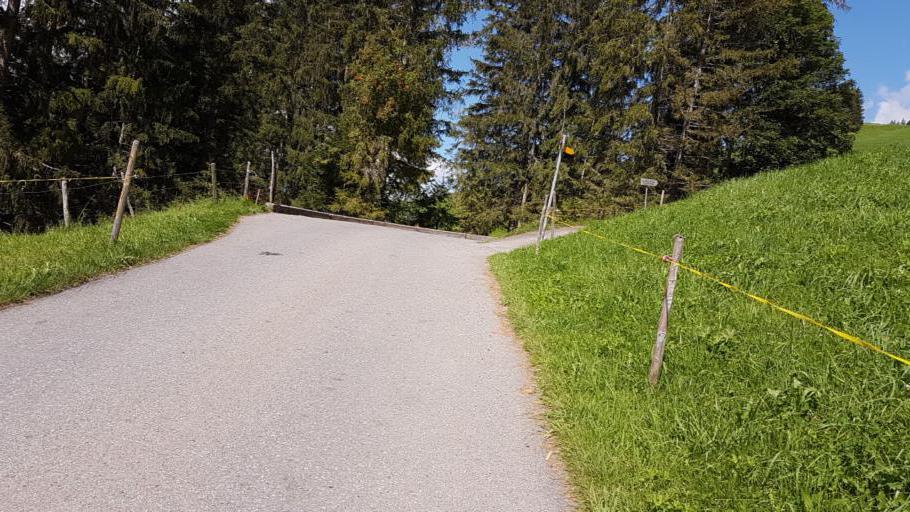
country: CH
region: Bern
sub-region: Frutigen-Niedersimmental District
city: Adelboden
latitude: 46.5030
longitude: 7.5894
